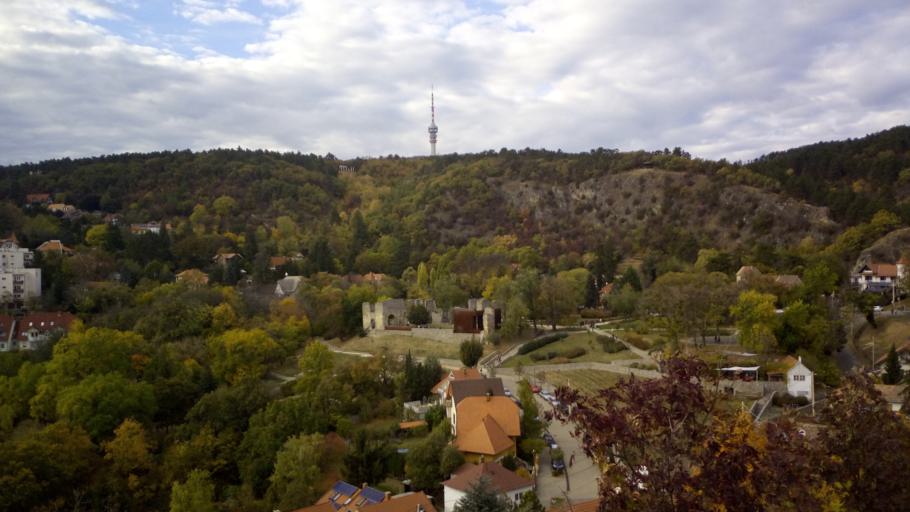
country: HU
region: Baranya
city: Pecs
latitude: 46.0857
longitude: 18.2377
